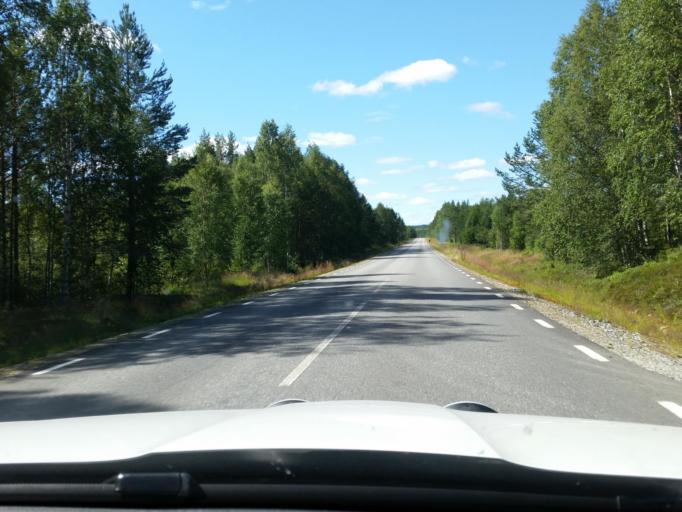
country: SE
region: Norrbotten
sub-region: Pitea Kommun
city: Roknas
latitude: 65.1940
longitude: 21.0928
